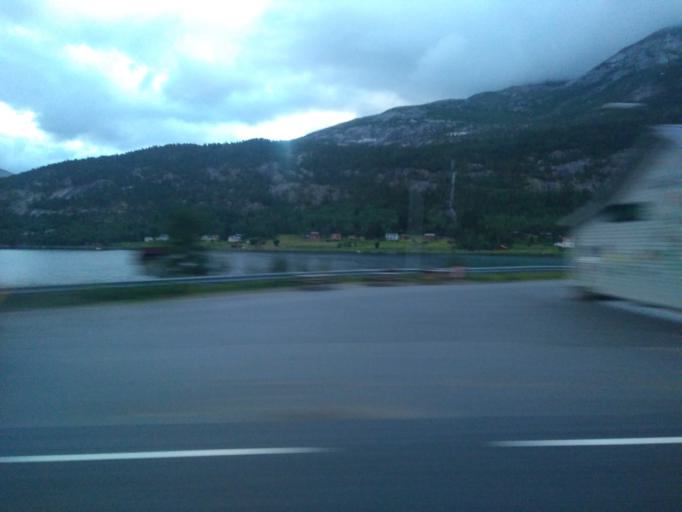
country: NO
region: Nordland
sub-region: Sorfold
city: Straumen
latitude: 67.7057
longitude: 15.8500
